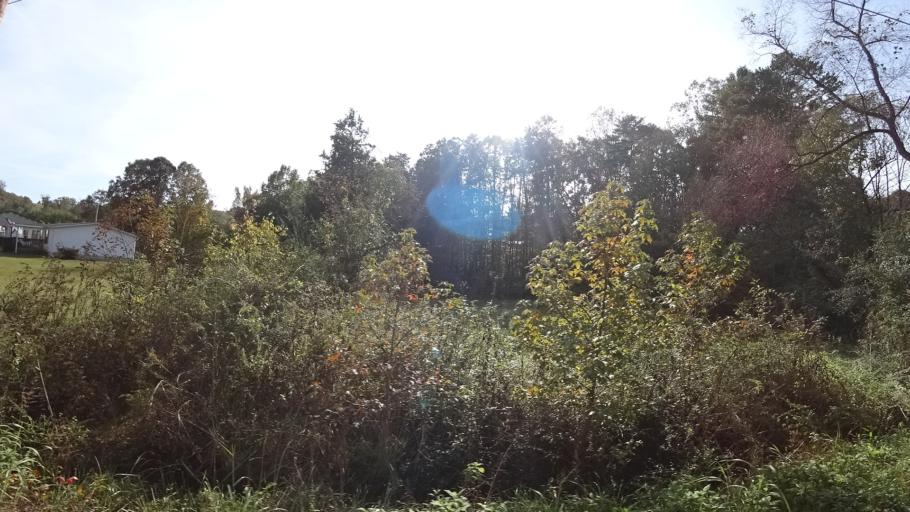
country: US
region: Tennessee
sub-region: Knox County
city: Farragut
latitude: 35.9174
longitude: -84.1788
